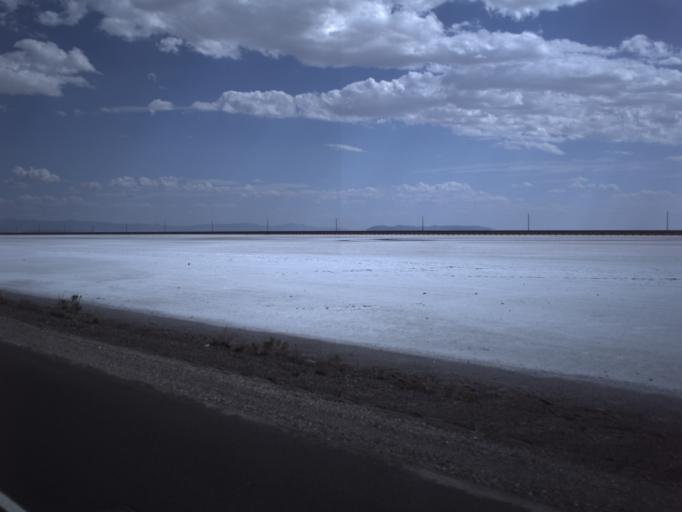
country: US
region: Utah
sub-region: Tooele County
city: Wendover
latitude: 40.7344
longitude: -113.6577
